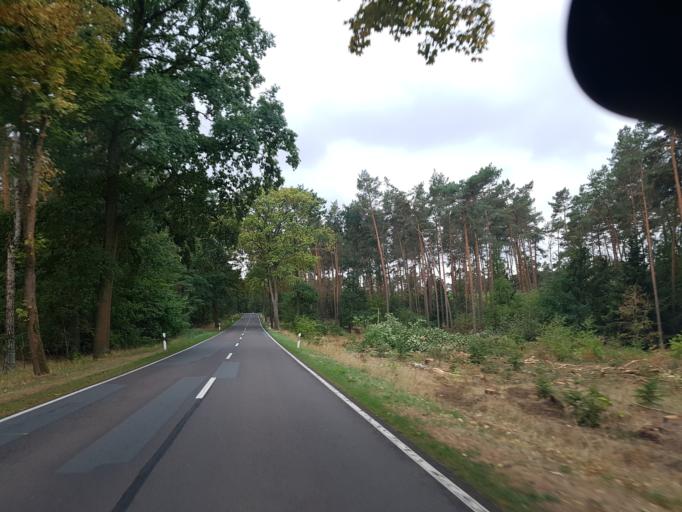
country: DE
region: Saxony-Anhalt
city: Loburg
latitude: 52.1454
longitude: 12.0944
